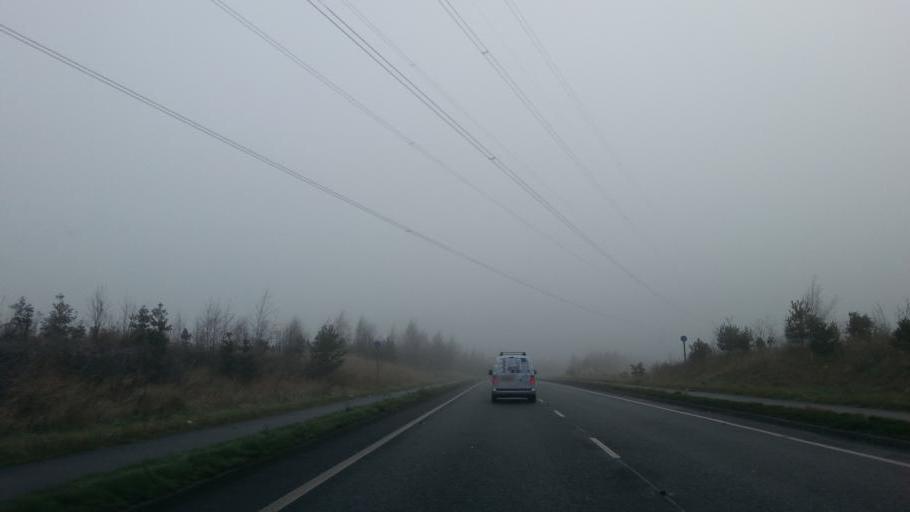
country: GB
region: England
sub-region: Cheshire East
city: Alderley Edge
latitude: 53.2883
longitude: -2.2528
